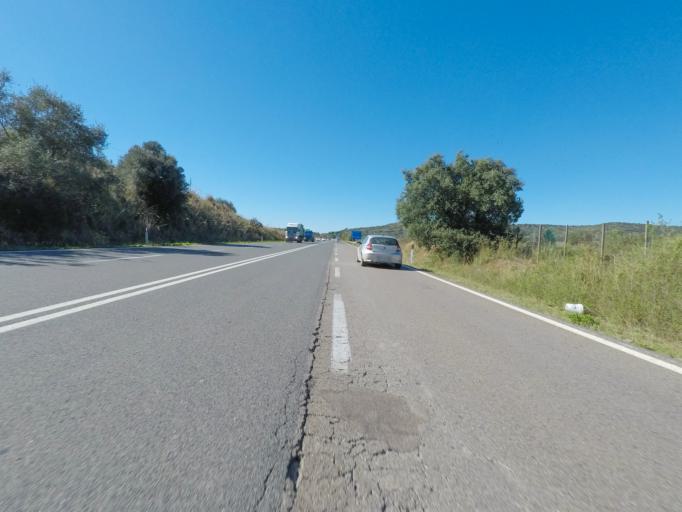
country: IT
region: Tuscany
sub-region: Provincia di Grosseto
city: Orbetello Scalo
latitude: 42.4166
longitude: 11.3121
